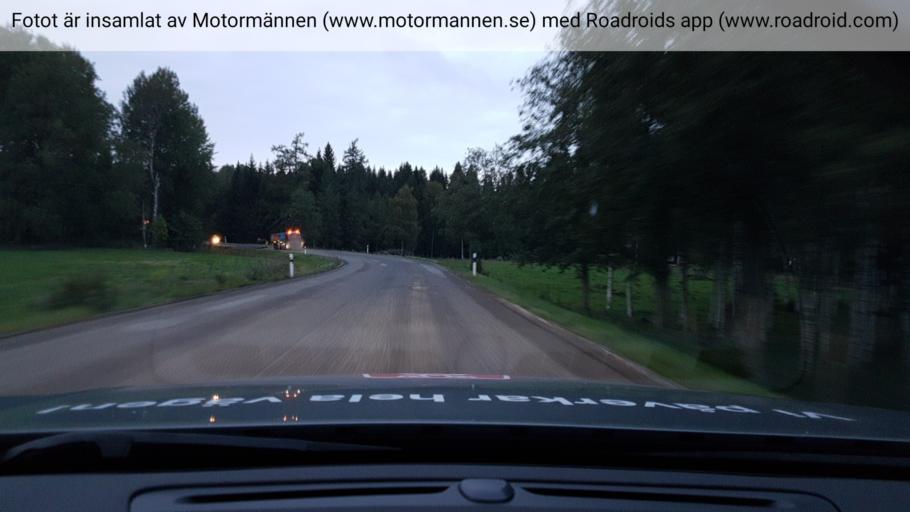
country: SE
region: OErebro
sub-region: Nora Kommun
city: As
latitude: 59.4616
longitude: 14.8664
